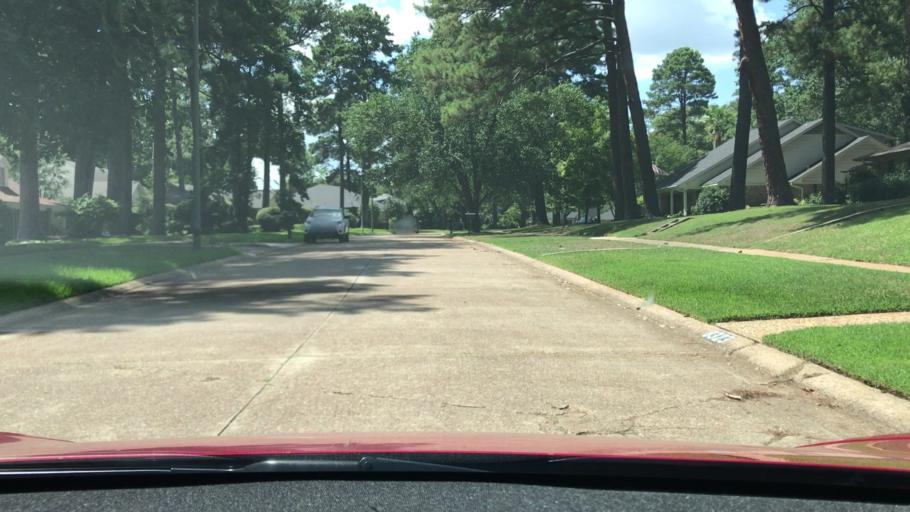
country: US
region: Louisiana
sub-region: Bossier Parish
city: Bossier City
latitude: 32.4297
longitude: -93.7341
